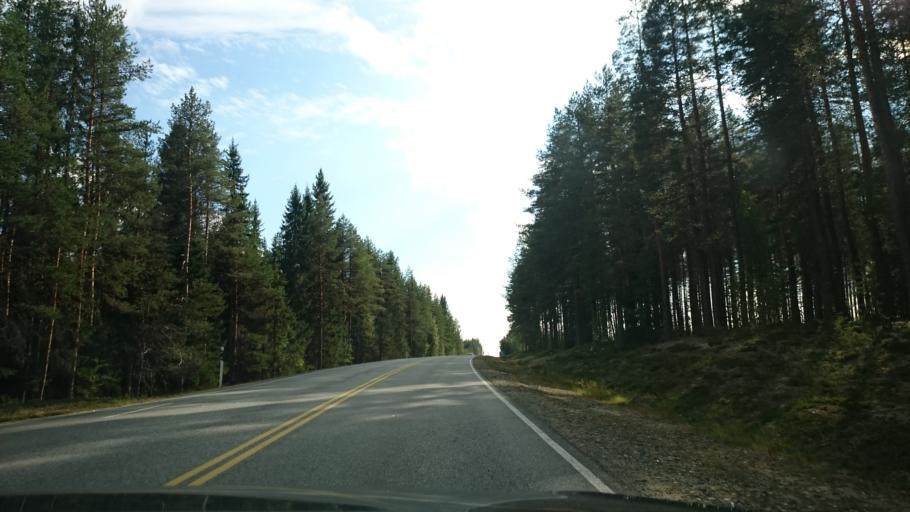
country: FI
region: Kainuu
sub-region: Kehys-Kainuu
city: Kuhmo
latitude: 64.5160
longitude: 29.9439
